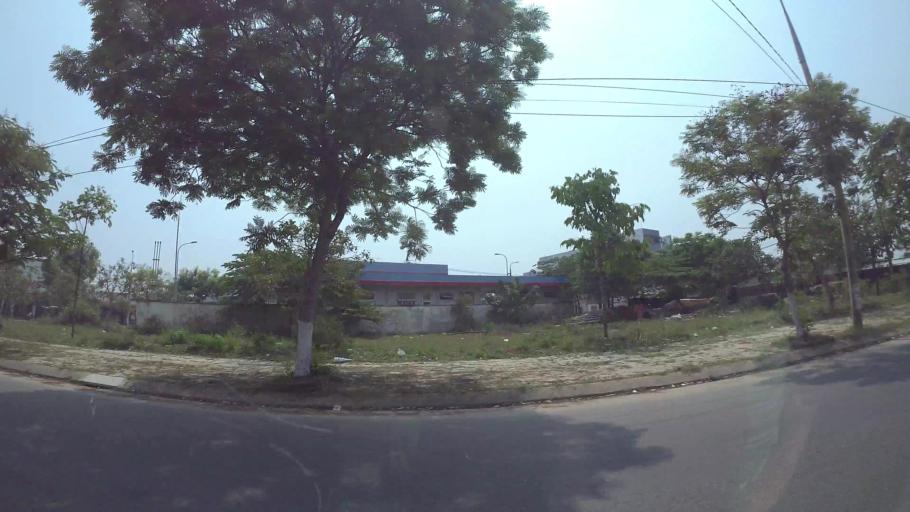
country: VN
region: Da Nang
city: Cam Le
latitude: 16.0044
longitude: 108.2067
